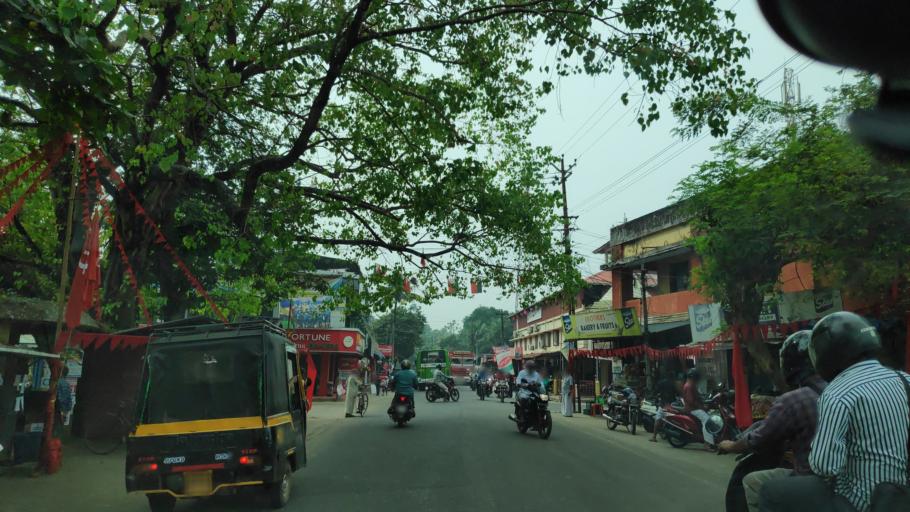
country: IN
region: Kerala
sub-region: Alappuzha
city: Alleppey
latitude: 9.5723
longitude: 76.3477
